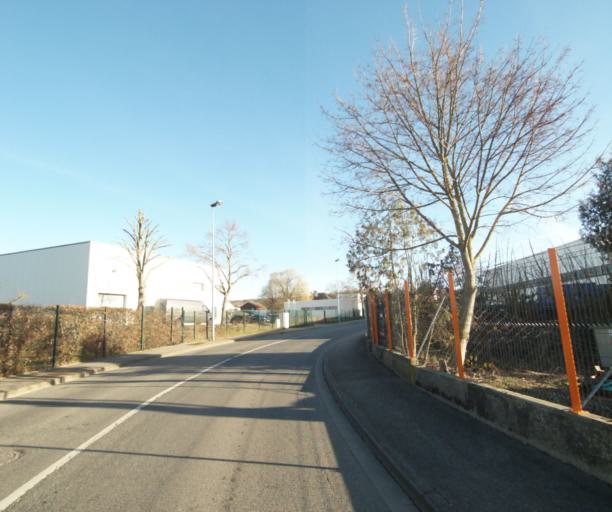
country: FR
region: Lorraine
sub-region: Departement de Meurthe-et-Moselle
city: Pulnoy
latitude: 48.7061
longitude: 6.2544
